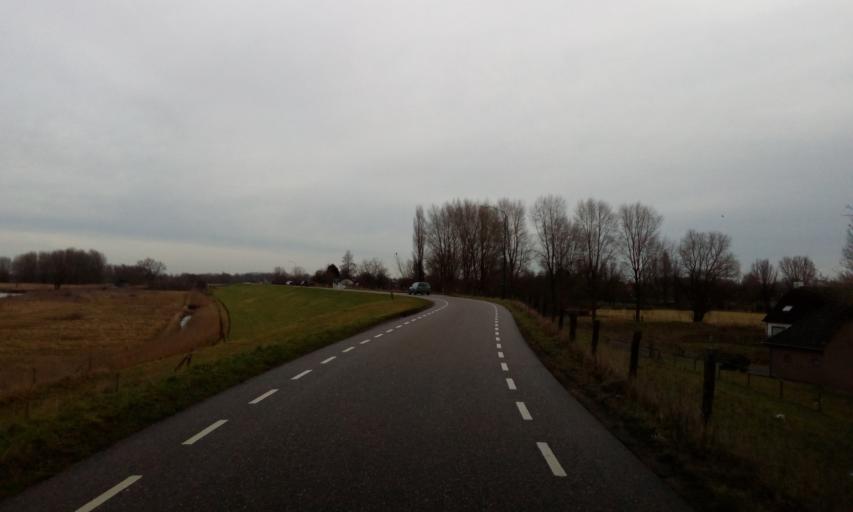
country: NL
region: South Holland
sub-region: Gemeente Gorinchem
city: Gorinchem
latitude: 51.8154
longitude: 4.9745
